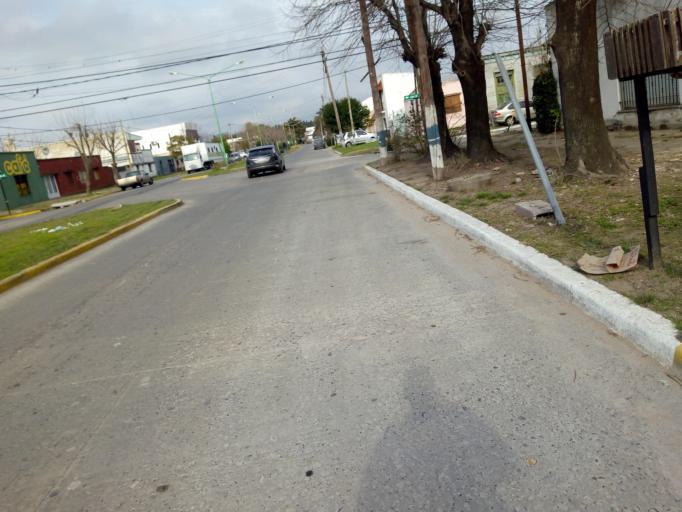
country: AR
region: Buenos Aires
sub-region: Partido de La Plata
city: La Plata
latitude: -34.8967
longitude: -57.9361
